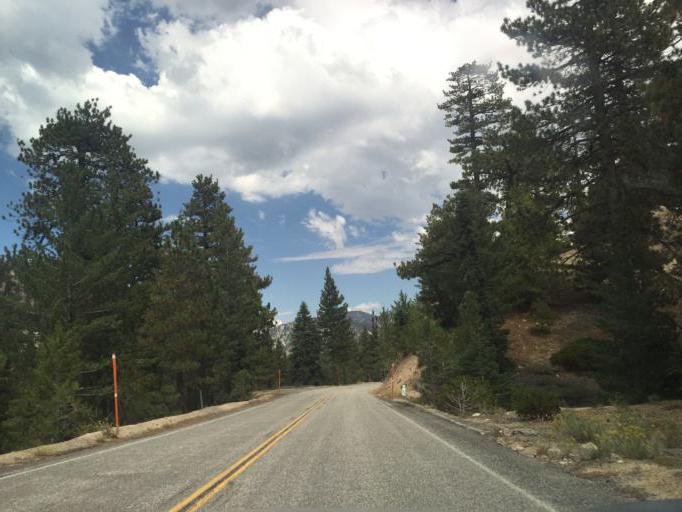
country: US
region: California
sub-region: Los Angeles County
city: Littlerock
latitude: 34.3434
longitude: -117.9175
